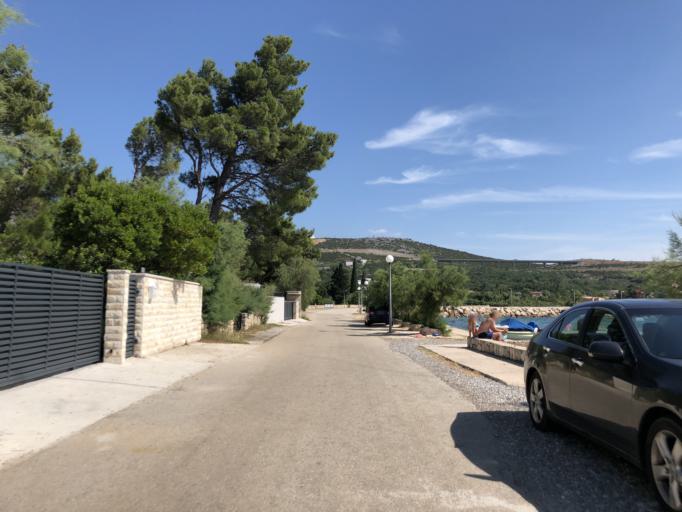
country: HR
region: Zadarska
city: Posedarje
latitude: 44.2509
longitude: 15.5370
